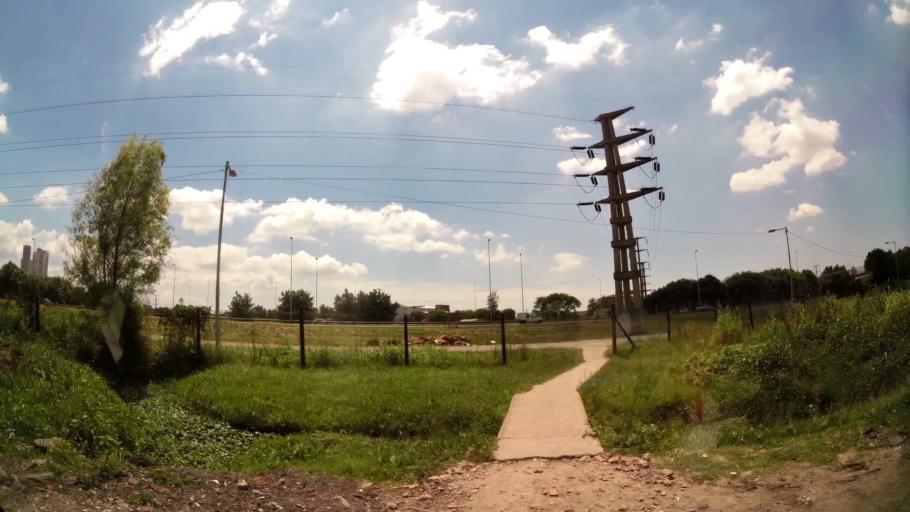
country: AR
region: Buenos Aires
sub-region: Partido de Tigre
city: Tigre
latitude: -34.4384
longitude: -58.5863
